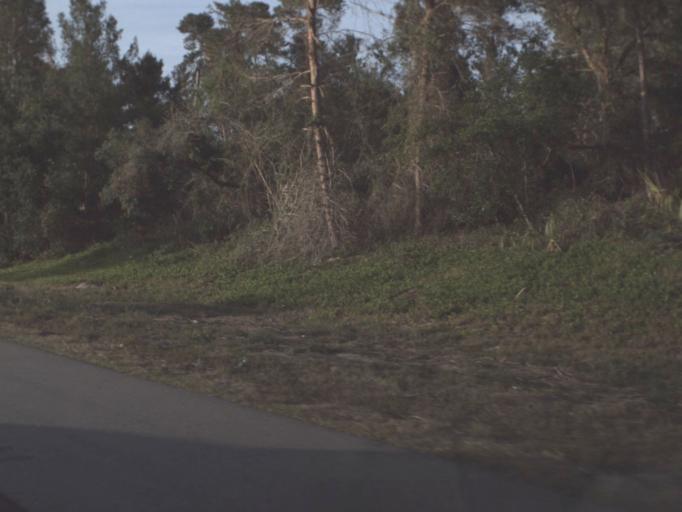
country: US
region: Florida
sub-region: Brevard County
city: Mims
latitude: 28.6256
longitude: -80.8529
